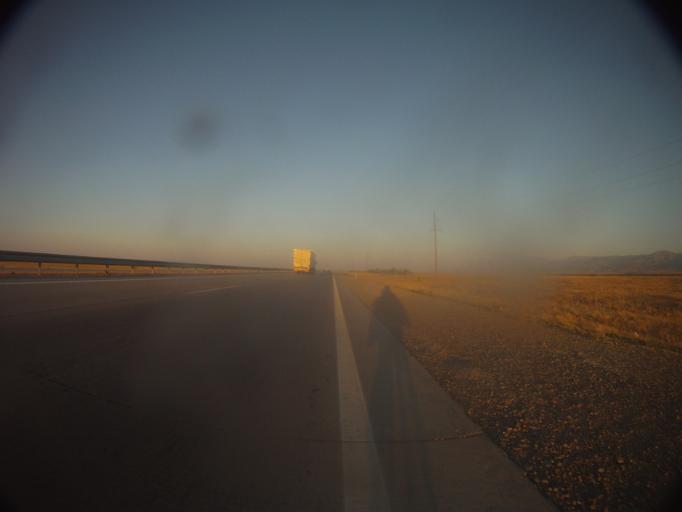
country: KZ
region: Zhambyl
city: Sarykemer
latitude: 43.0116
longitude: 71.6708
